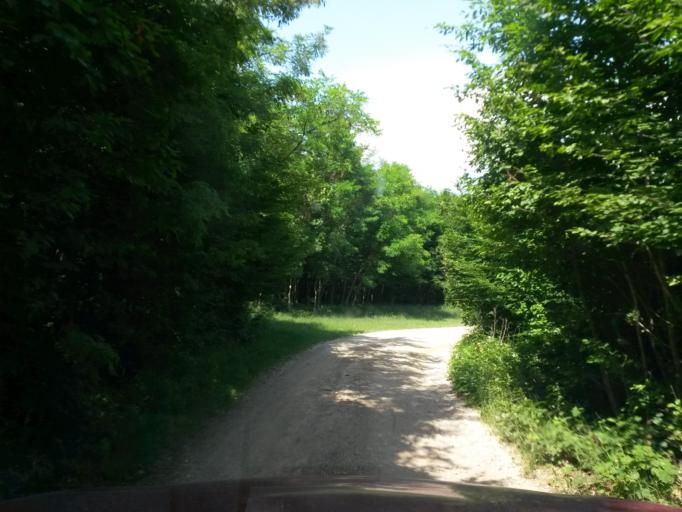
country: SK
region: Kosicky
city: Moldava nad Bodvou
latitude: 48.6460
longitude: 20.9584
